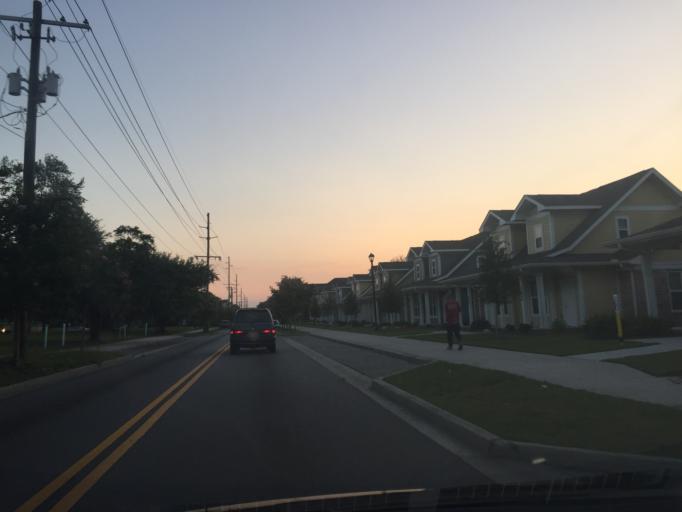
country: US
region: Georgia
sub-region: Chatham County
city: Thunderbolt
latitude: 32.0582
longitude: -81.0616
